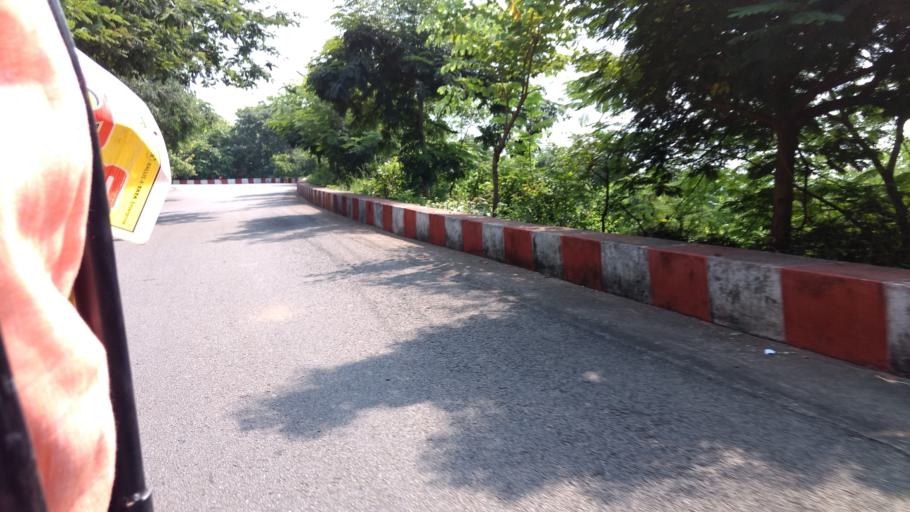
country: IN
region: Andhra Pradesh
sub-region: East Godavari
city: Tuni
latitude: 17.2800
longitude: 82.3990
